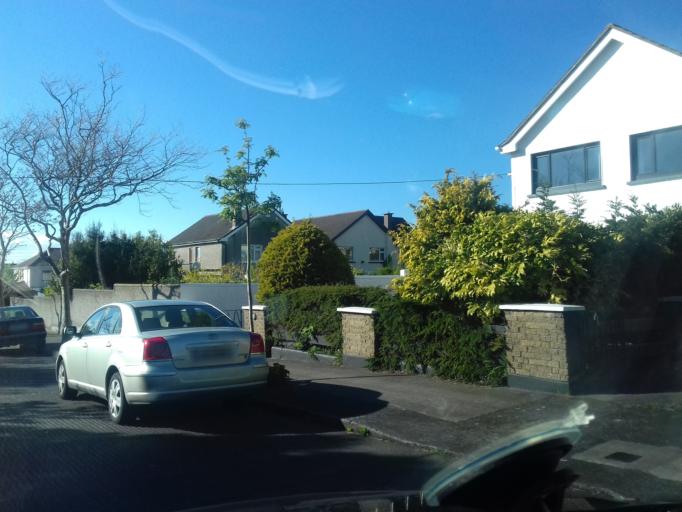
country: IE
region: Leinster
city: Sutton
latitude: 53.3769
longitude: -6.0962
